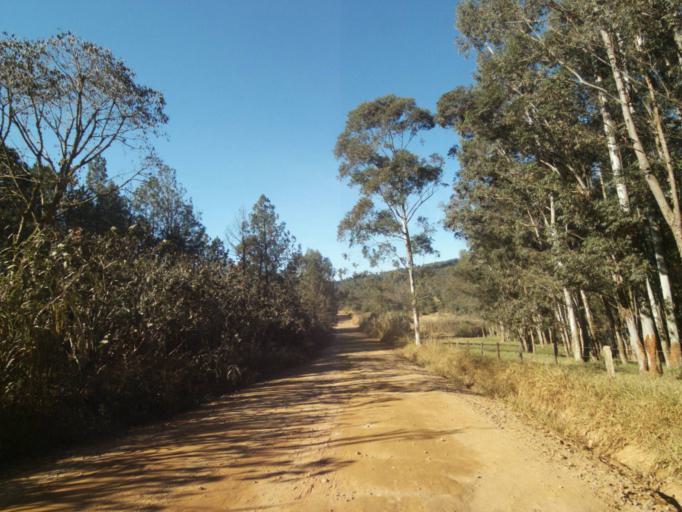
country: BR
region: Parana
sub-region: Tibagi
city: Tibagi
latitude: -24.5315
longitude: -50.3777
